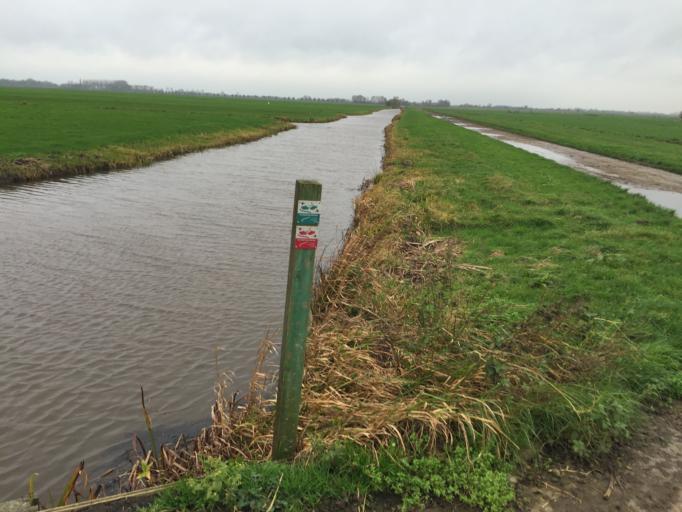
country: NL
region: Utrecht
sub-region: Gemeente Woerden
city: Woerden
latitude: 52.1033
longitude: 4.8870
